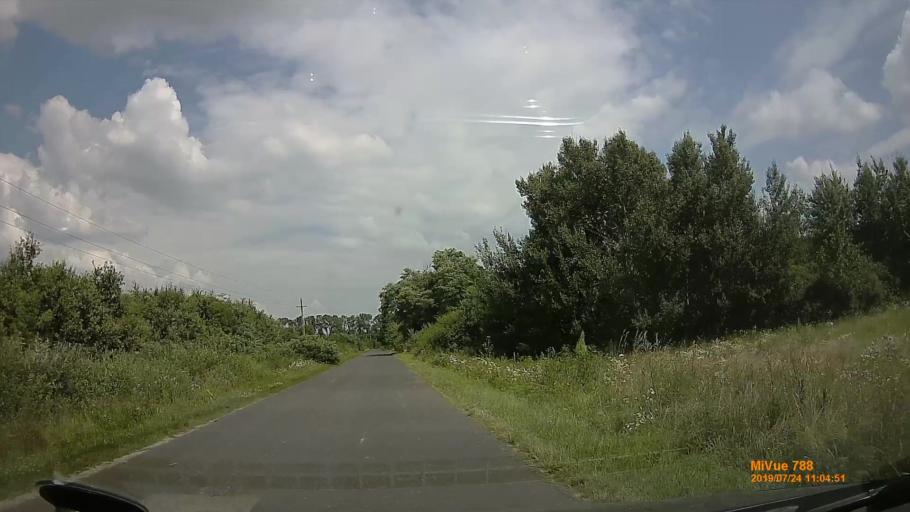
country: HU
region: Szabolcs-Szatmar-Bereg
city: Tarpa
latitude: 48.1742
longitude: 22.5164
